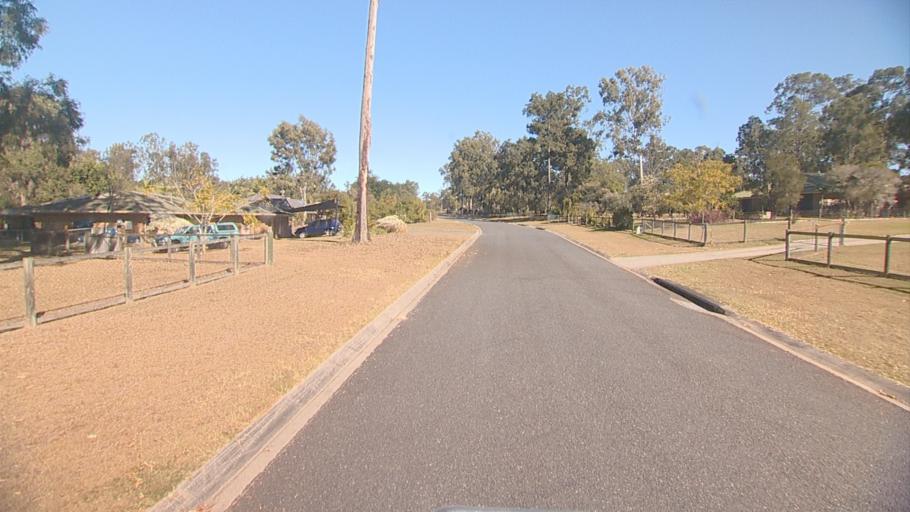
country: AU
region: Queensland
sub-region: Logan
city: North Maclean
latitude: -27.8188
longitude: 152.9486
